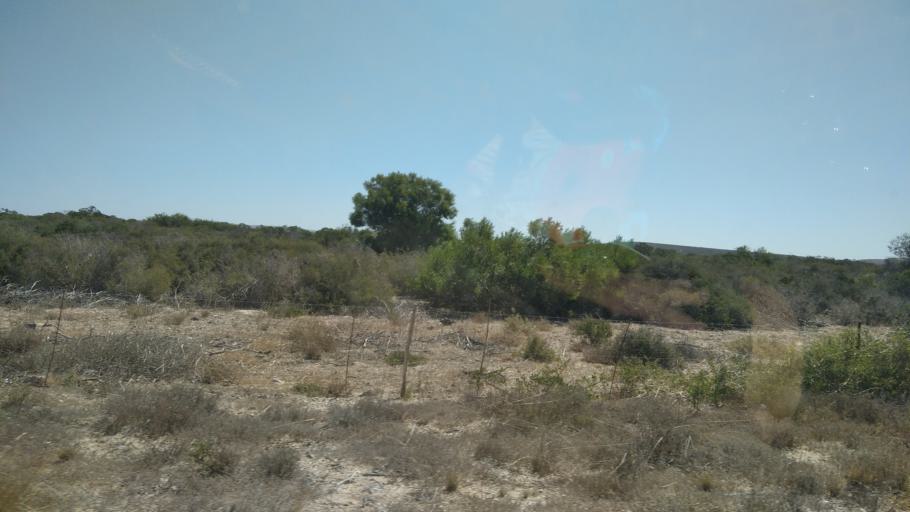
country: ZA
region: Western Cape
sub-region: West Coast District Municipality
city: Vredenburg
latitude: -32.9966
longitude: 18.1299
